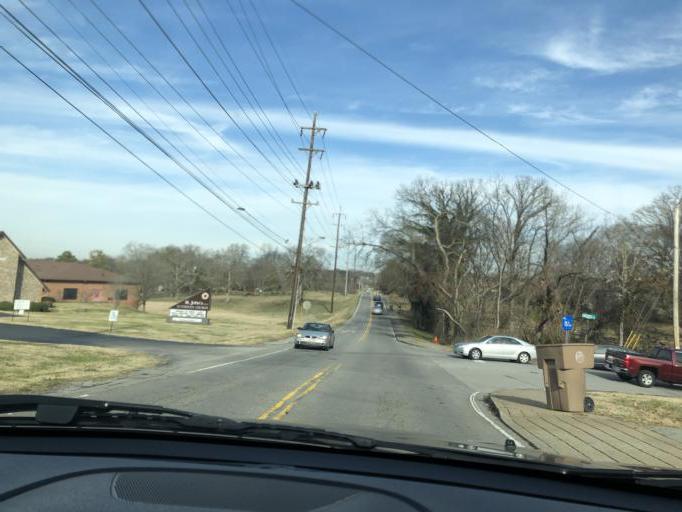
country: US
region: Tennessee
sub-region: Davidson County
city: Lakewood
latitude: 36.1775
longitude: -86.6785
